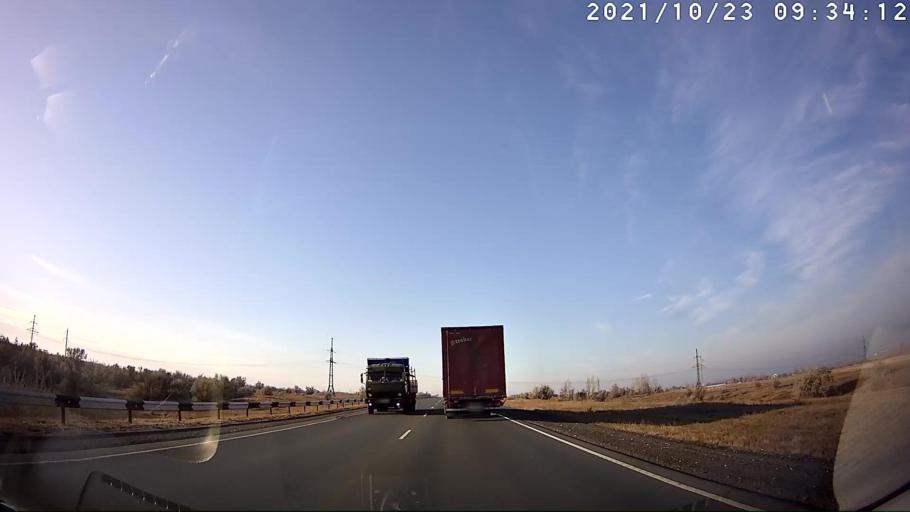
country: RU
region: Saratov
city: Sokolovyy
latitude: 51.6554
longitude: 45.8388
